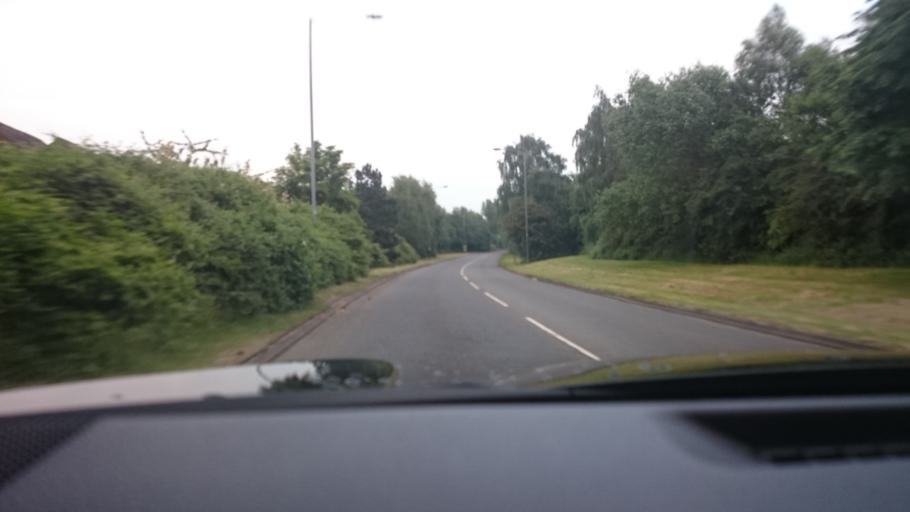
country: GB
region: England
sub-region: Warwickshire
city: Stratford-upon-Avon
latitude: 52.1844
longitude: -1.7120
